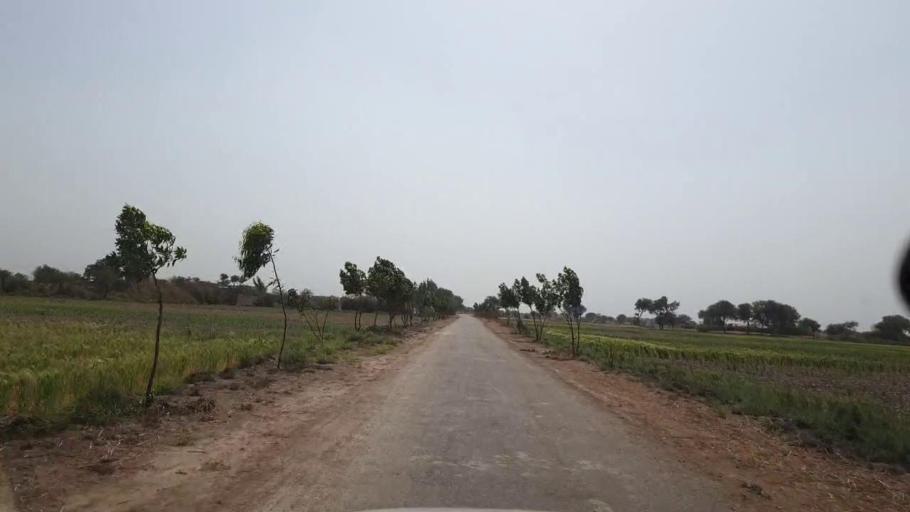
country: PK
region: Sindh
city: Matli
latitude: 25.0434
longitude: 68.6859
